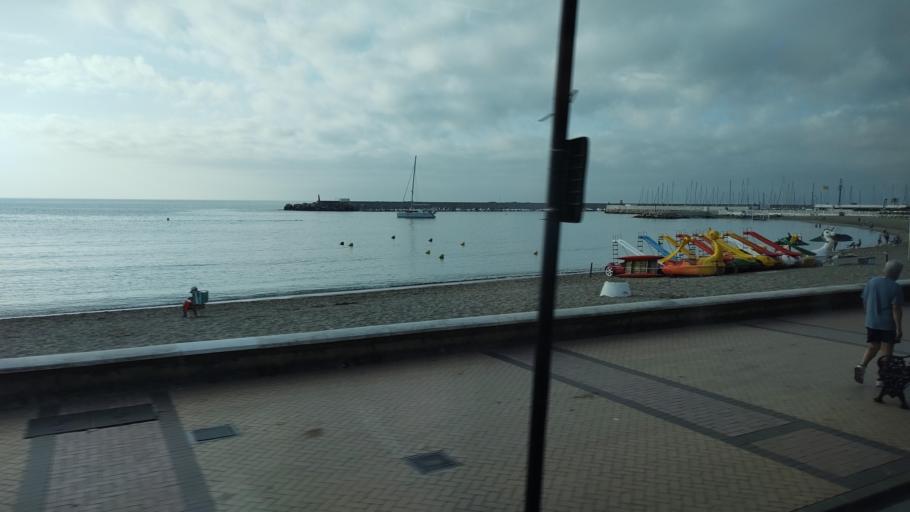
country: ES
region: Andalusia
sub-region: Provincia de Malaga
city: Fuengirola
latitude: 36.5456
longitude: -4.6173
